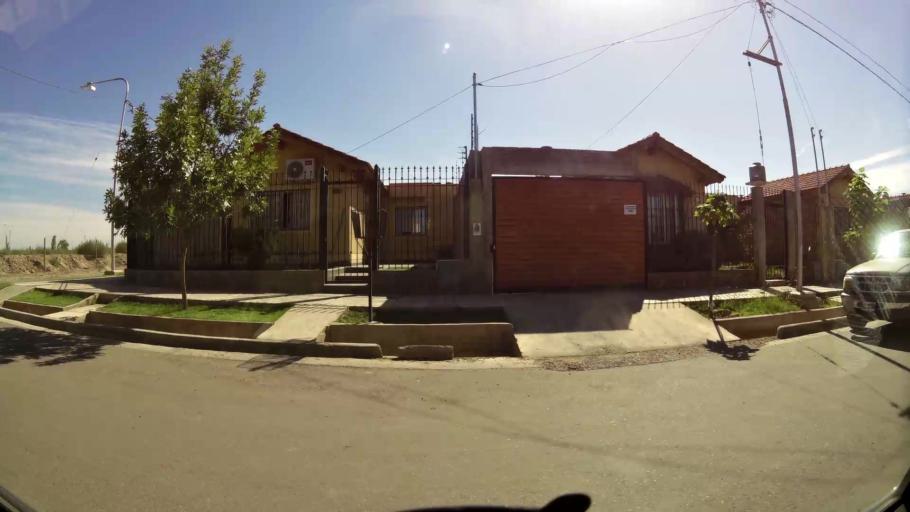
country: AR
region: Mendoza
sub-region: Departamento de Godoy Cruz
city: Godoy Cruz
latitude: -32.9523
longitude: -68.8141
